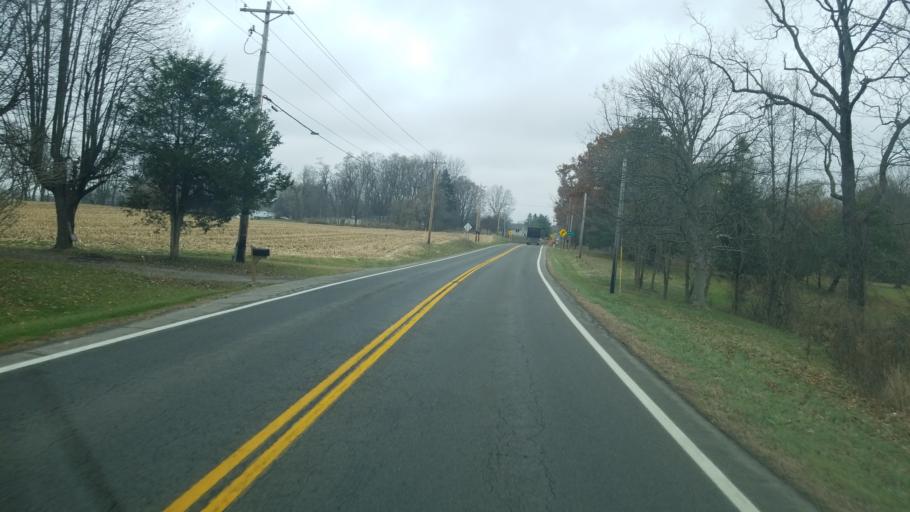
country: US
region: Ohio
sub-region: Huron County
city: Greenwich
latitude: 41.0902
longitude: -82.4883
